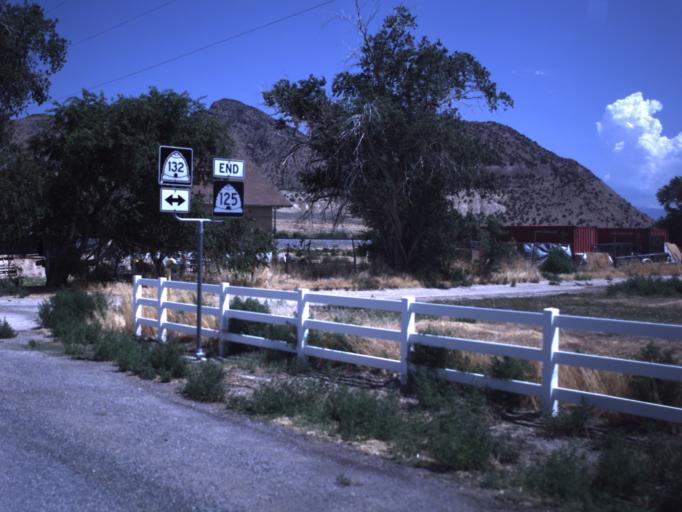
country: US
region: Utah
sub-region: Millard County
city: Delta
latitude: 39.5355
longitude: -112.2734
